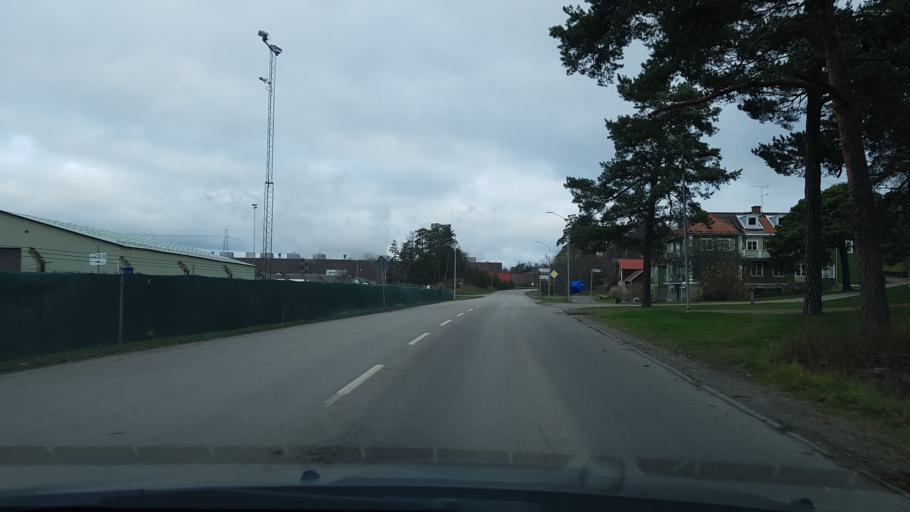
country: SE
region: Stockholm
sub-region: Norrtalje Kommun
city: Hallstavik
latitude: 60.0552
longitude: 18.5945
